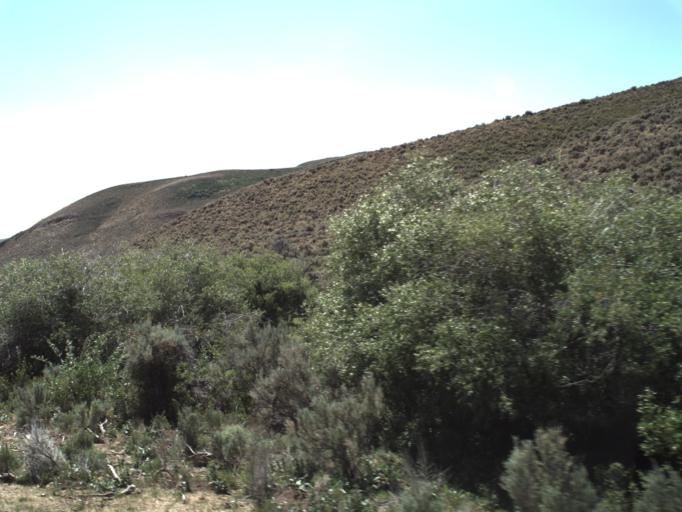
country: US
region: Utah
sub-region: Rich County
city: Randolph
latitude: 41.4995
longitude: -111.3214
